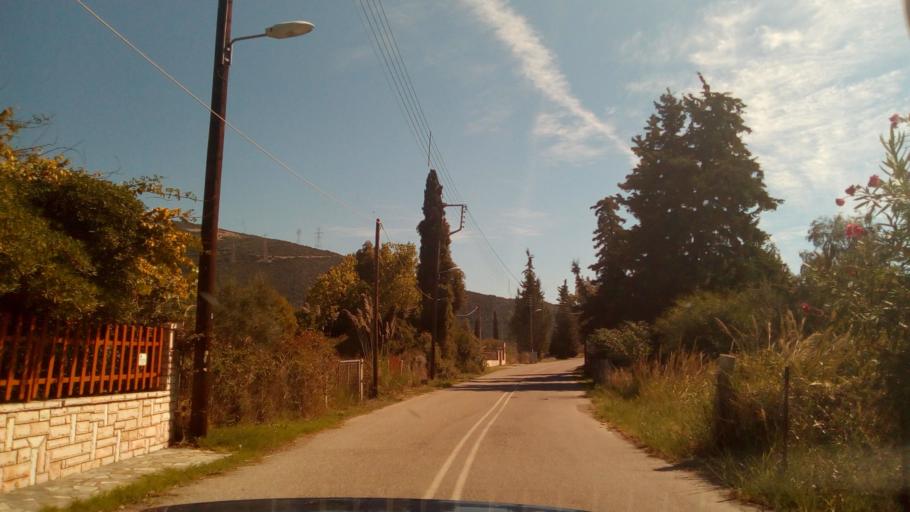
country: GR
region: West Greece
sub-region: Nomos Achaias
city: Selianitika
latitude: 38.3750
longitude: 22.0852
